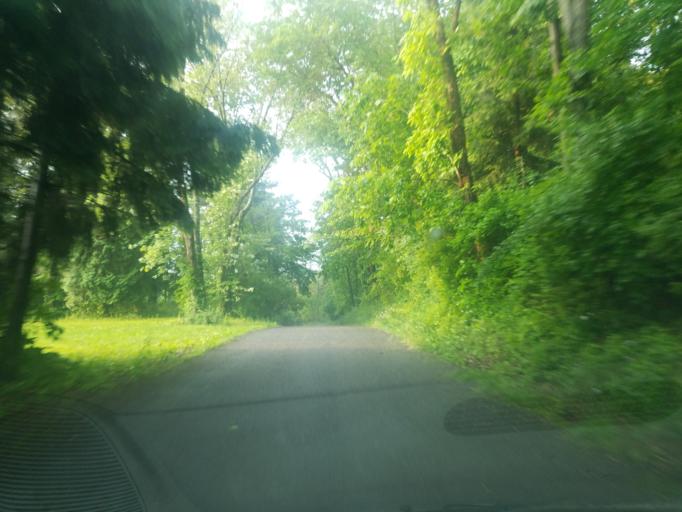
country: US
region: Ohio
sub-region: Stark County
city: Minerva
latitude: 40.7393
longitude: -80.9809
